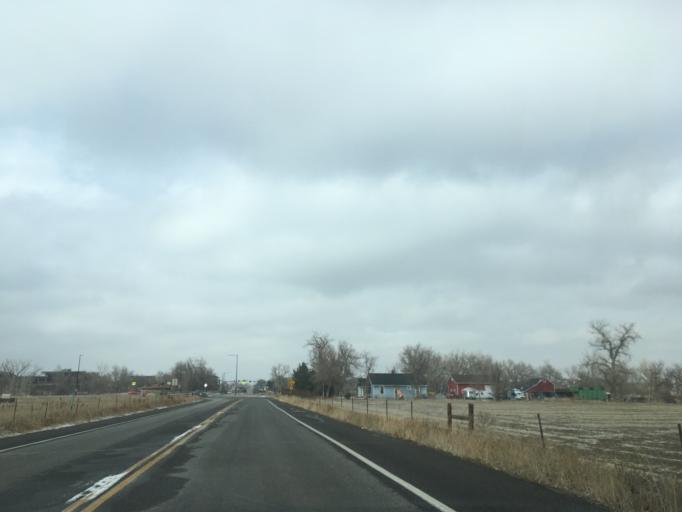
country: US
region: Colorado
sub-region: Boulder County
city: Lafayette
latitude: 39.9774
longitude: -105.0905
